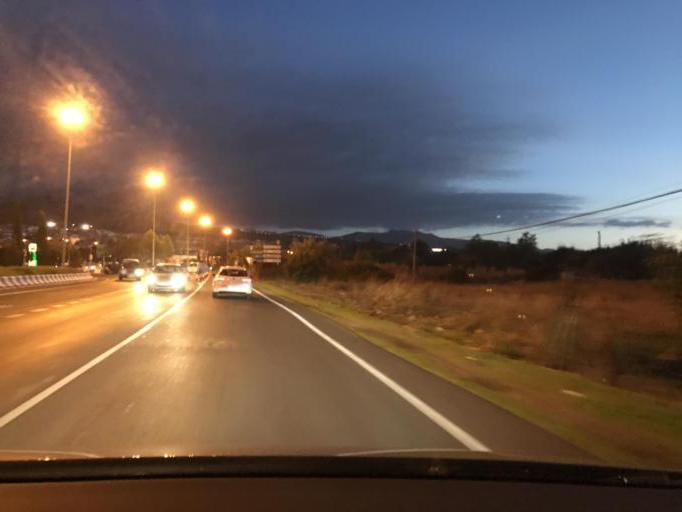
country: ES
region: Andalusia
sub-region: Provincia de Granada
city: Zubia
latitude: 37.1300
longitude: -3.5864
